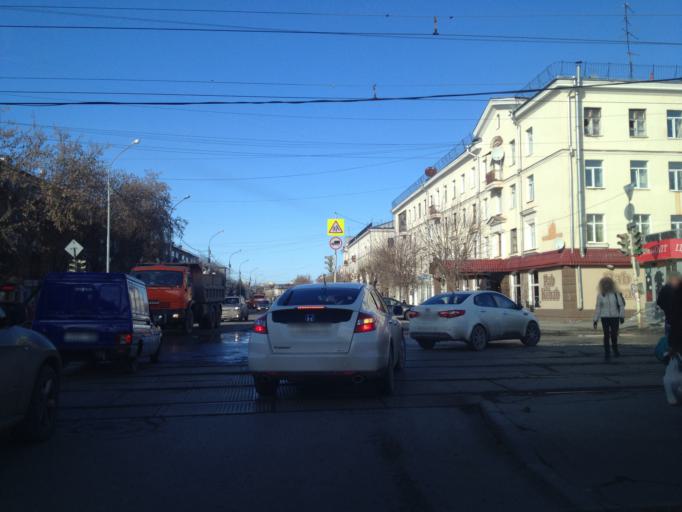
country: RU
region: Sverdlovsk
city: Yekaterinburg
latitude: 56.8358
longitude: 60.5531
